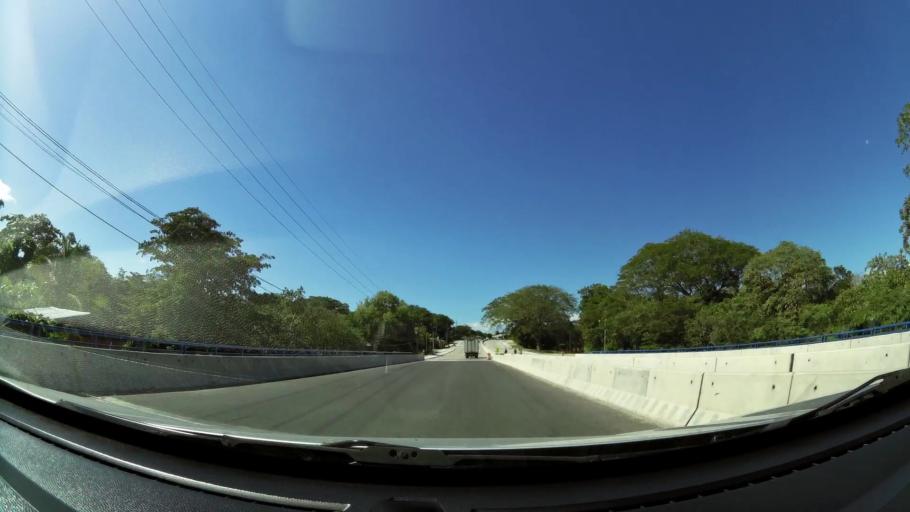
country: CR
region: Guanacaste
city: Liberia
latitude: 10.5650
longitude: -85.3879
